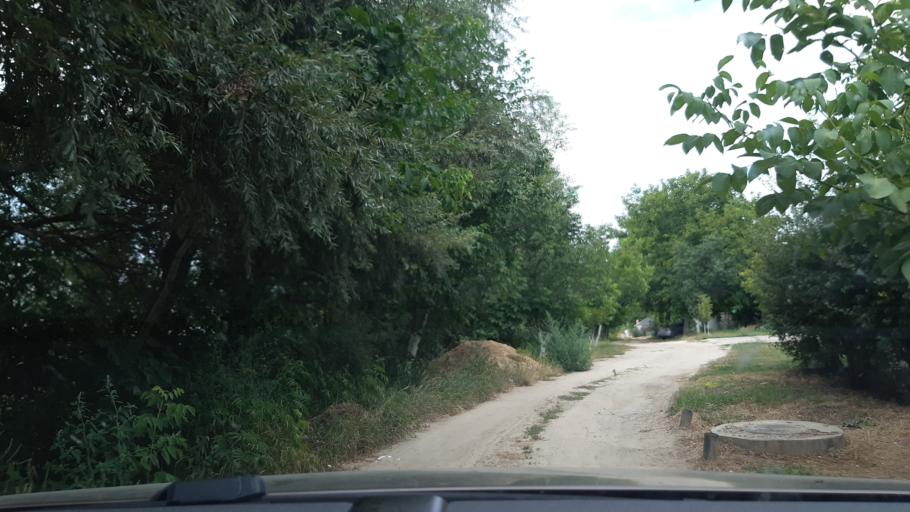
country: MD
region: Chisinau
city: Vatra
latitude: 47.0586
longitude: 28.7326
